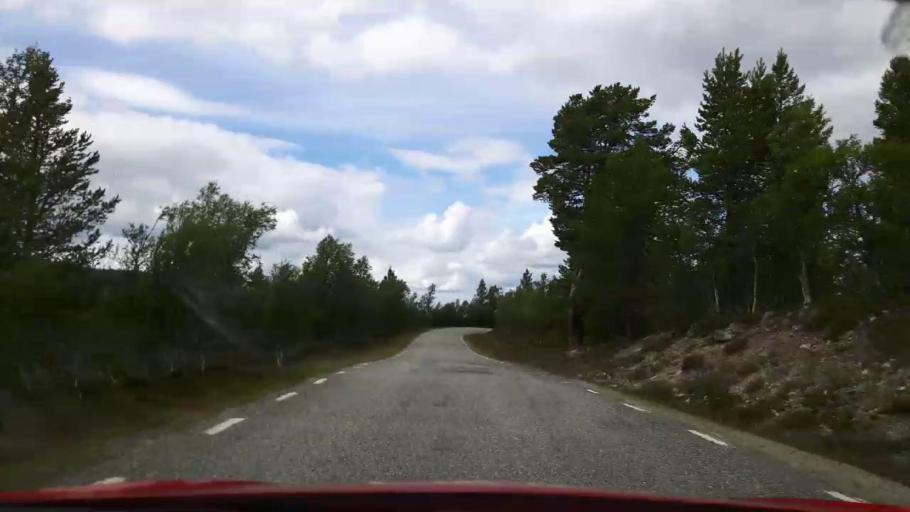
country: NO
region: Hedmark
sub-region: Engerdal
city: Engerdal
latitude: 62.3453
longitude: 12.7963
